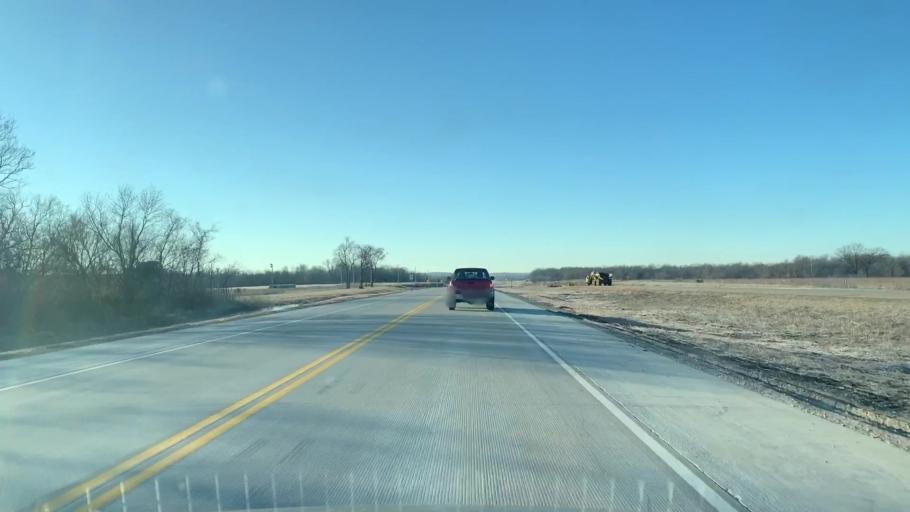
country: US
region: Kansas
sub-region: Bourbon County
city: Fort Scott
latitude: 37.7198
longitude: -94.7042
